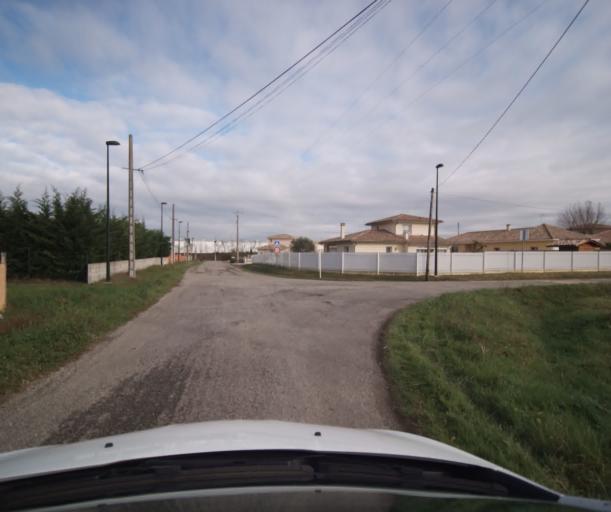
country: FR
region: Midi-Pyrenees
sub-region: Departement de la Haute-Garonne
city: Lespinasse
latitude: 43.7231
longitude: 1.3929
